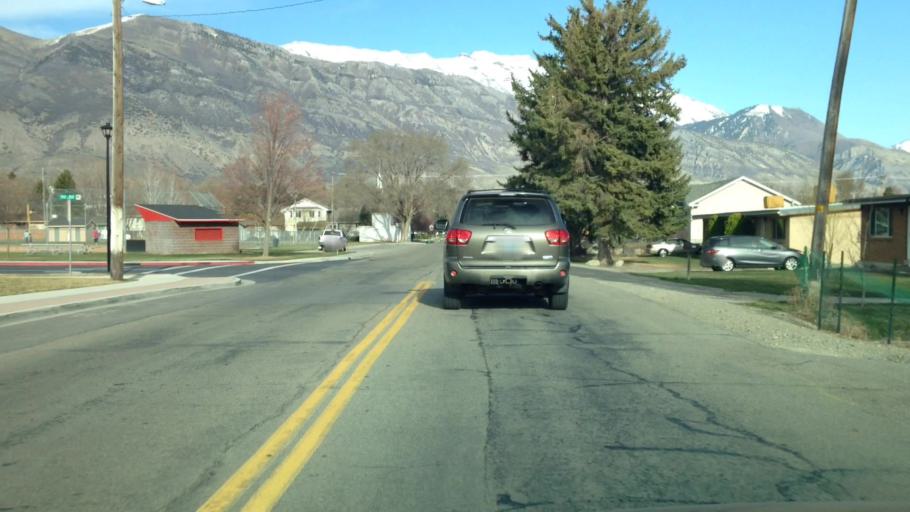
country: US
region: Utah
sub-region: Utah County
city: American Fork
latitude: 40.3918
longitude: -111.7844
